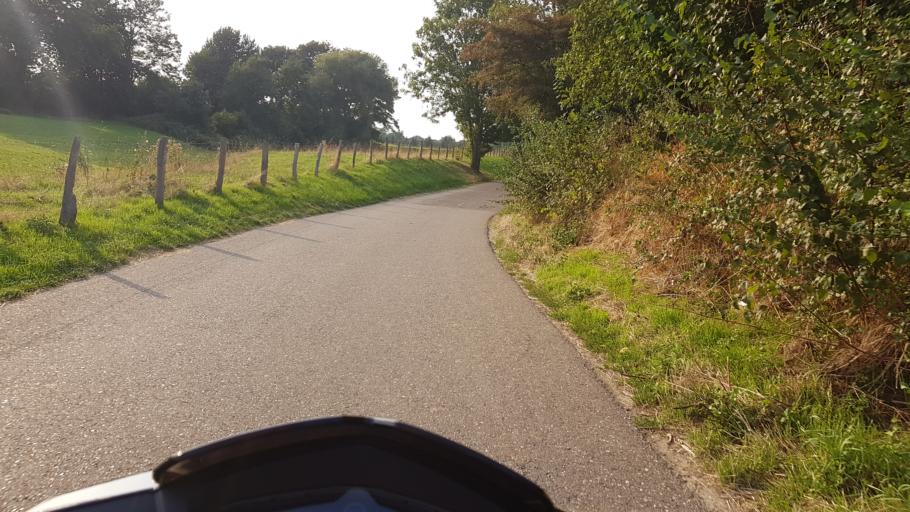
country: NL
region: Limburg
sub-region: Gemeente Stein
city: Elsloo
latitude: 50.9375
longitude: 5.7763
